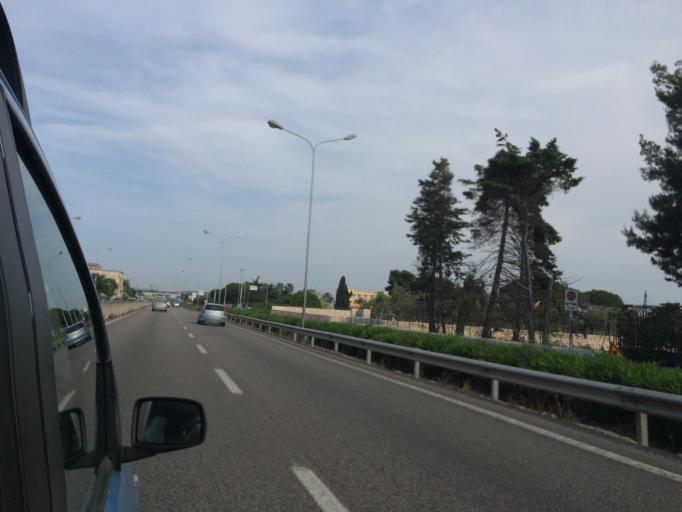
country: IT
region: Apulia
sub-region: Provincia di Bari
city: Triggiano
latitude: 41.0994
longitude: 16.9335
